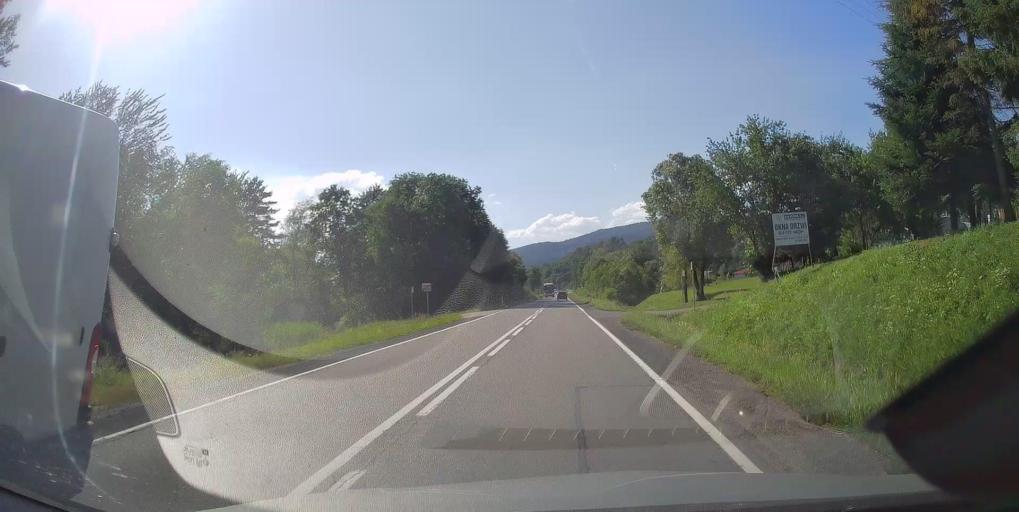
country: PL
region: Lesser Poland Voivodeship
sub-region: Powiat nowosadecki
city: Labowa
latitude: 49.5224
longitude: 20.8752
